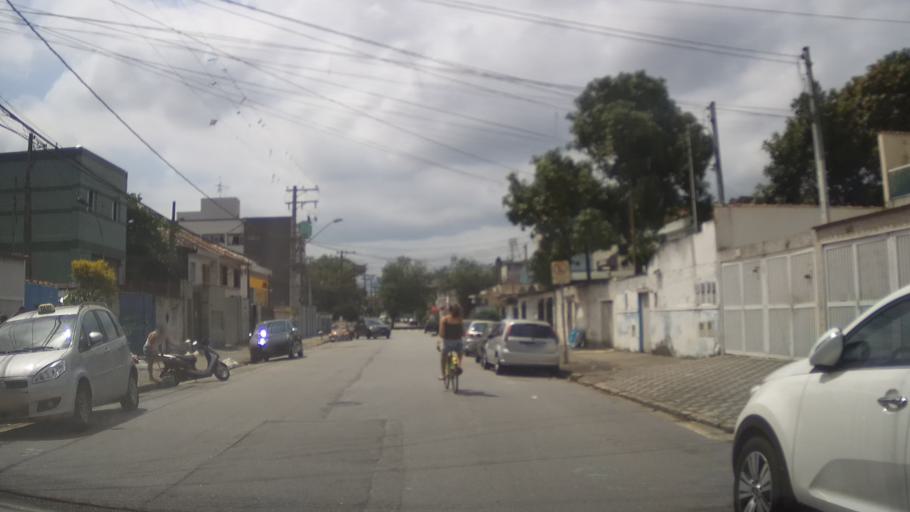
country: BR
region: Sao Paulo
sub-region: Santos
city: Santos
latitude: -23.9617
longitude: -46.3114
